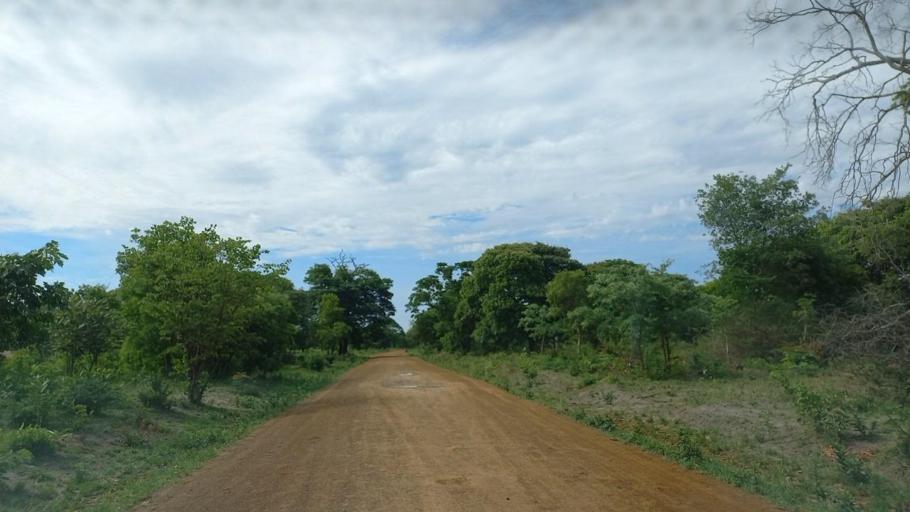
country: ZM
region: North-Western
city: Kabompo
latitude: -13.4569
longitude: 24.4271
